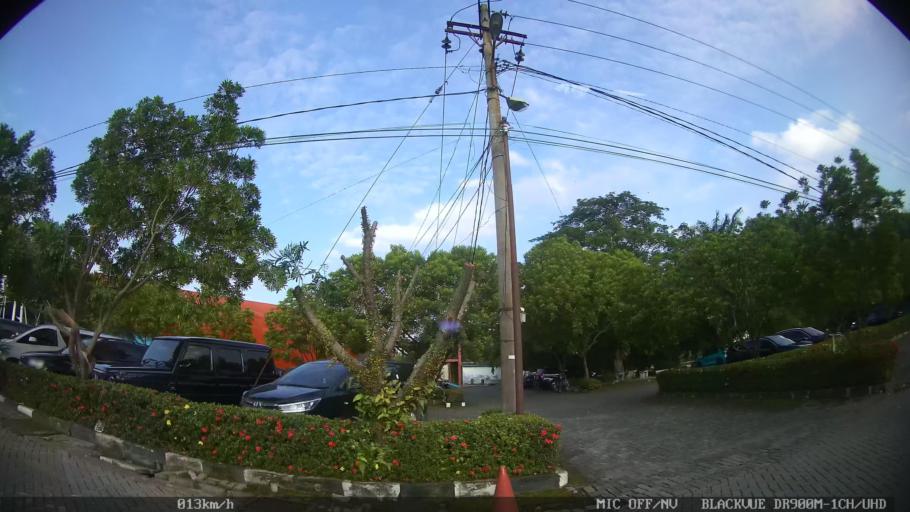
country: ID
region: North Sumatra
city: Medan
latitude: 3.6214
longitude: 98.6431
